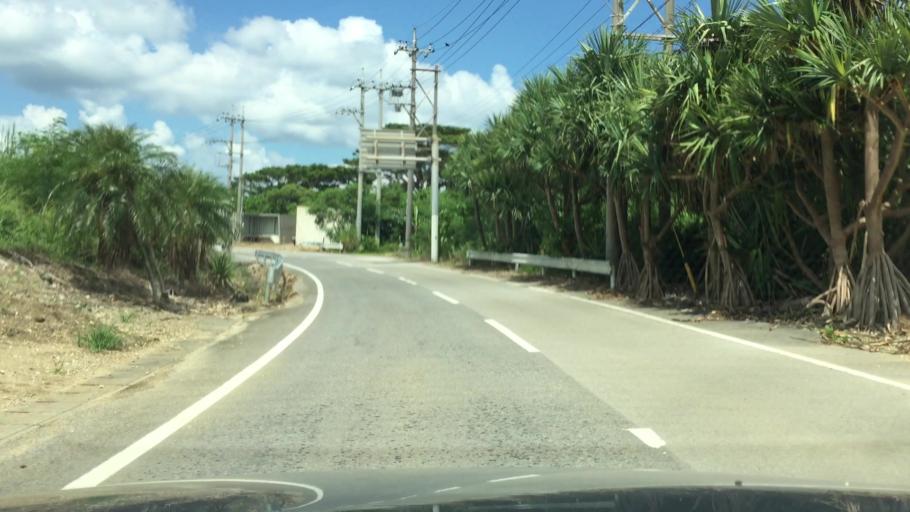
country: JP
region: Okinawa
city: Ishigaki
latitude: 24.3952
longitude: 124.1543
